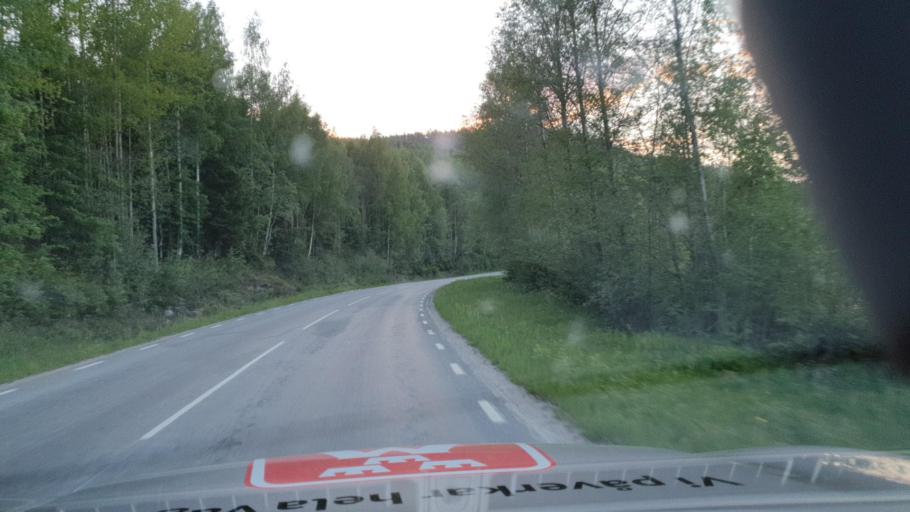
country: SE
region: Vaesternorrland
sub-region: OErnskoeldsviks Kommun
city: Ornskoldsvik
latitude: 63.2369
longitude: 18.6580
